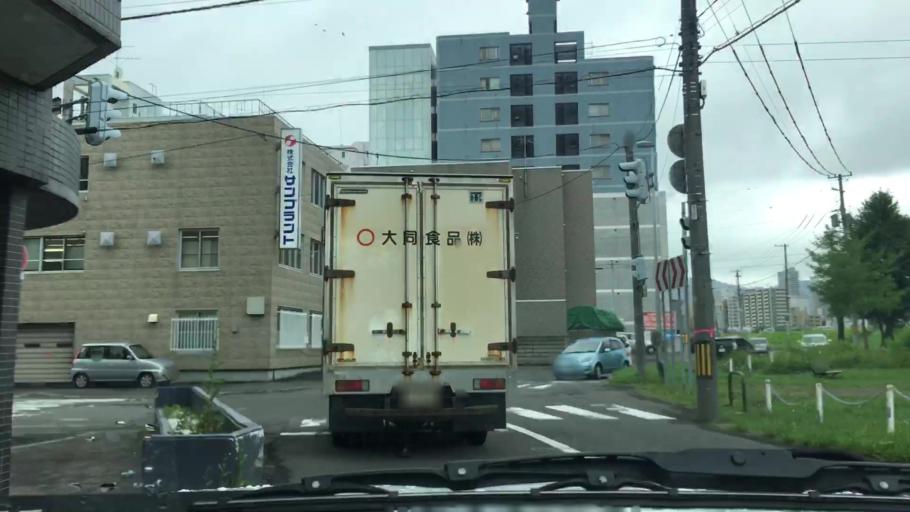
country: JP
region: Hokkaido
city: Sapporo
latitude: 43.0571
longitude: 141.3679
